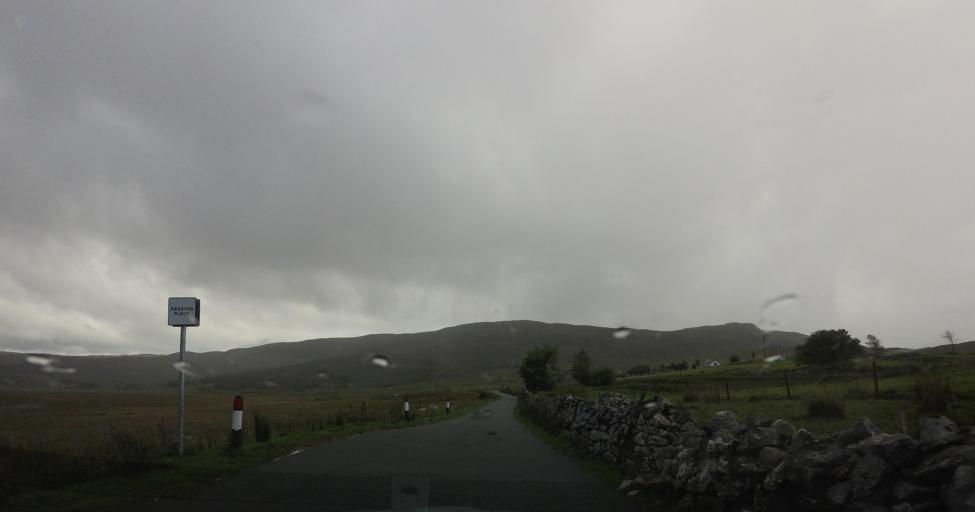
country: GB
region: Scotland
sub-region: Highland
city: Portree
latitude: 57.2099
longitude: -5.9877
